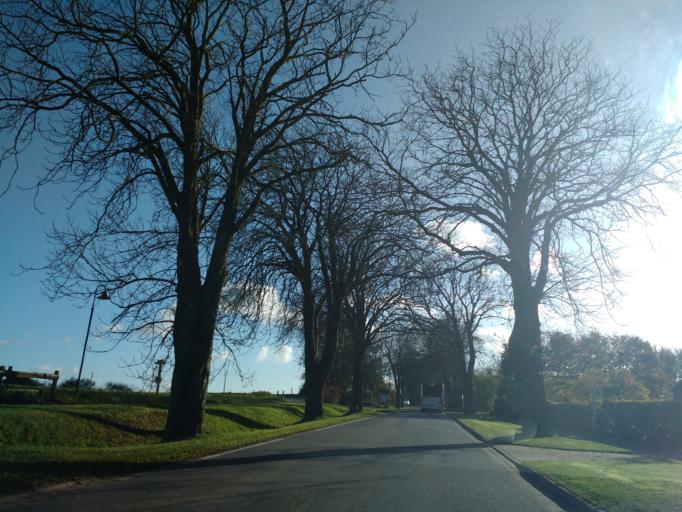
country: DE
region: Mecklenburg-Vorpommern
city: Klutz
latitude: 53.9248
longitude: 11.1549
